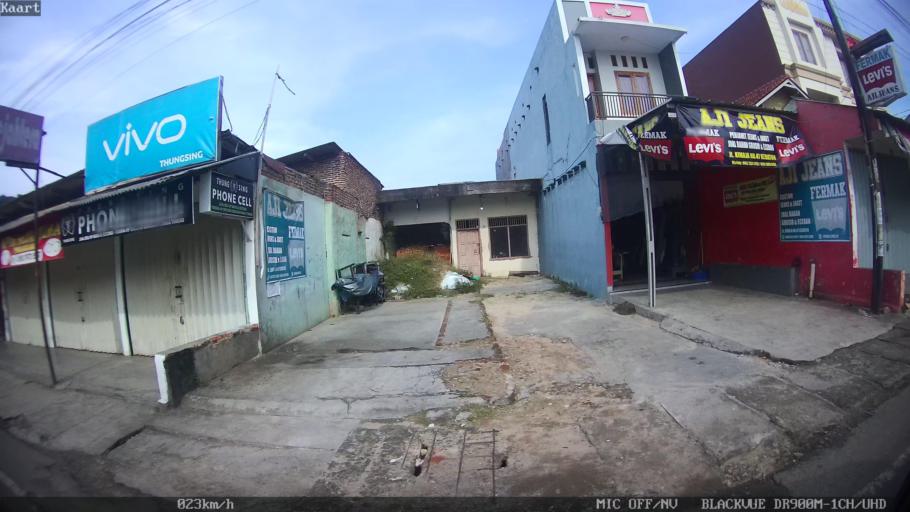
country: ID
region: Lampung
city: Kedaton
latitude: -5.3856
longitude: 105.2706
